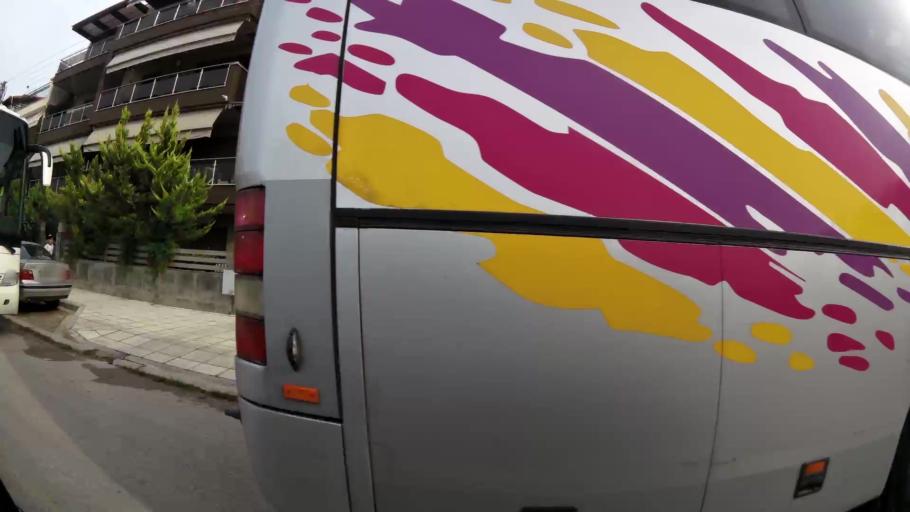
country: GR
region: Central Macedonia
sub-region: Nomos Thessalonikis
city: Thermi
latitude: 40.5463
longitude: 23.0246
